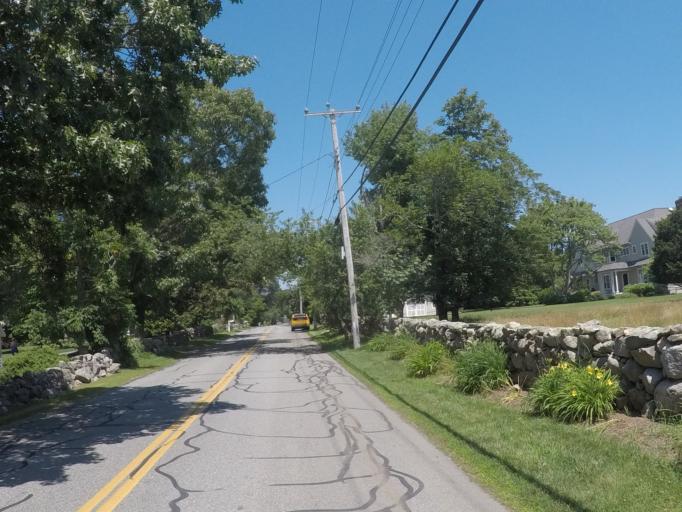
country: US
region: Massachusetts
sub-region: Bristol County
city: Bliss Corner
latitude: 41.5379
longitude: -70.9516
